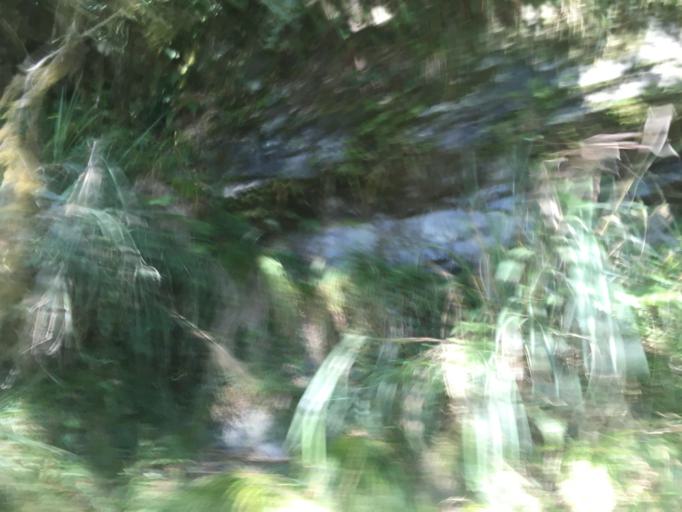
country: TW
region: Taiwan
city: Daxi
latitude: 24.6092
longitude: 121.4592
